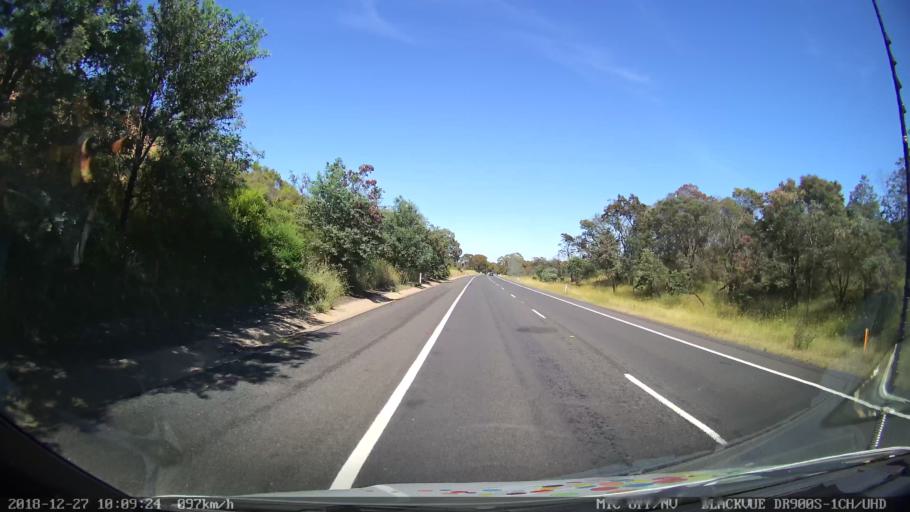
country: AU
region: New South Wales
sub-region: Lithgow
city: Portland
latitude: -33.4510
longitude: 149.8097
